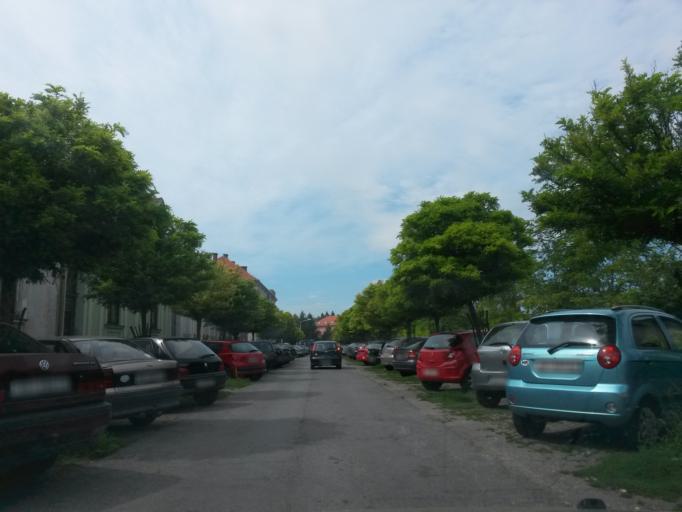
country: HR
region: Osjecko-Baranjska
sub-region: Grad Osijek
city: Osijek
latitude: 45.5582
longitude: 18.7103
